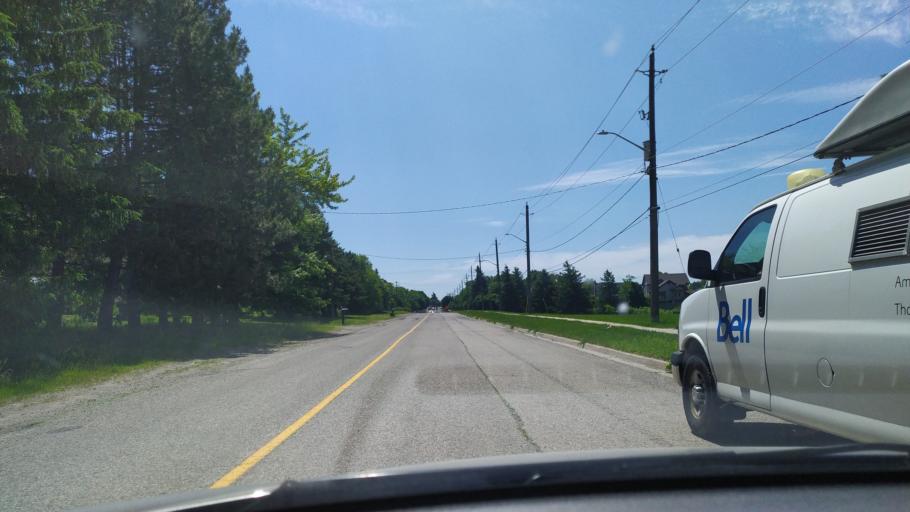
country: CA
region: Ontario
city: Waterloo
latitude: 43.4530
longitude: -80.5713
